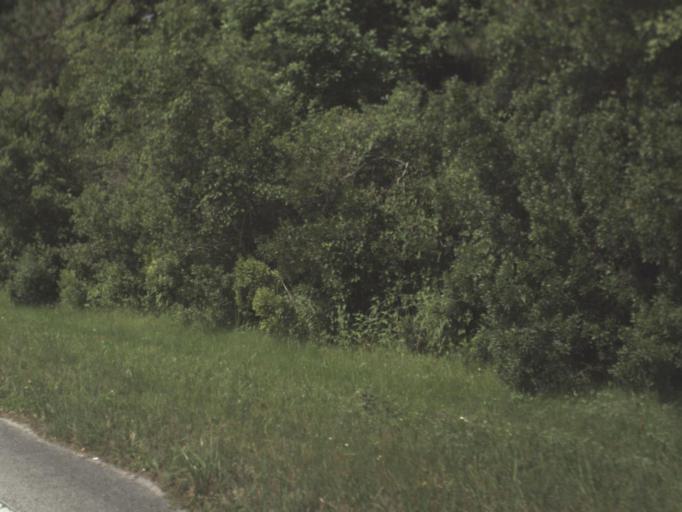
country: US
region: Florida
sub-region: Bradford County
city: Starke
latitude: 29.9450
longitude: -82.0163
